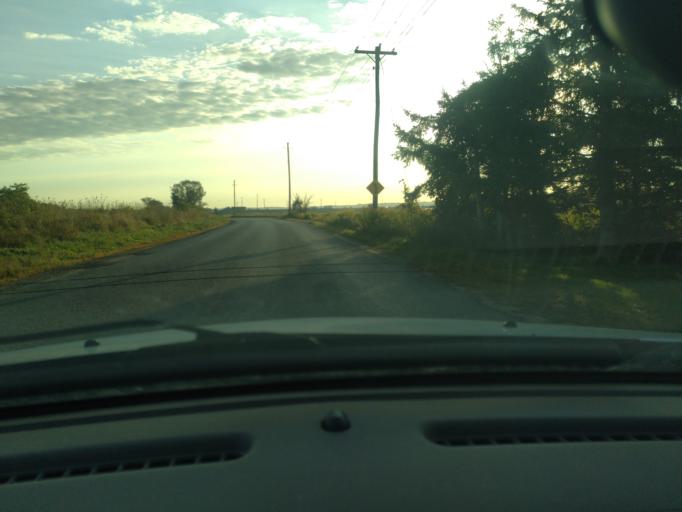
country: CA
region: Ontario
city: Bradford West Gwillimbury
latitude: 44.0496
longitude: -79.6150
